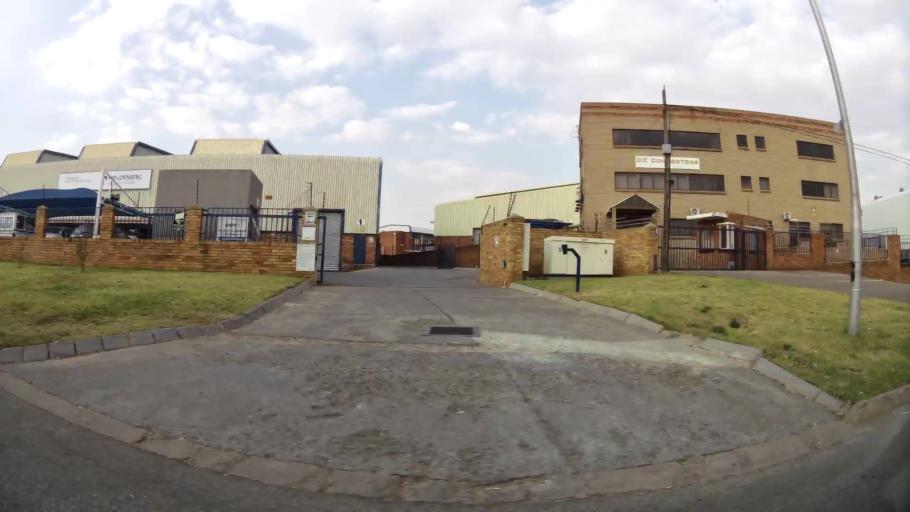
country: ZA
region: Gauteng
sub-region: City of Johannesburg Metropolitan Municipality
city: Modderfontein
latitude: -26.1472
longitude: 28.1823
